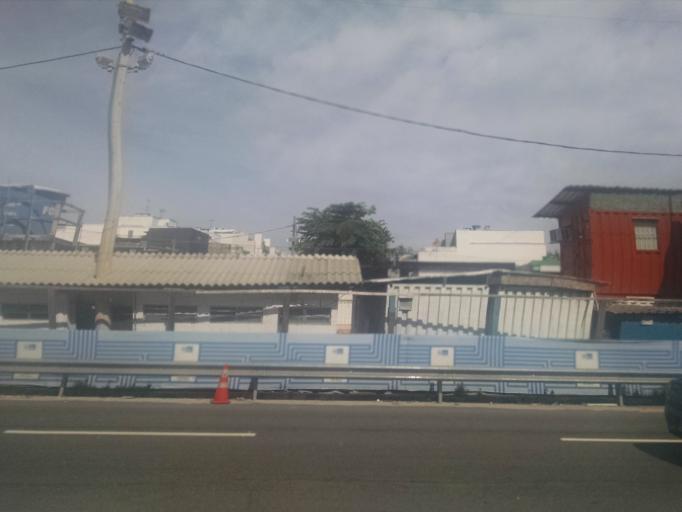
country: BR
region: Rio de Janeiro
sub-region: Rio De Janeiro
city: Rio de Janeiro
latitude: -23.0071
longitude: -43.3076
